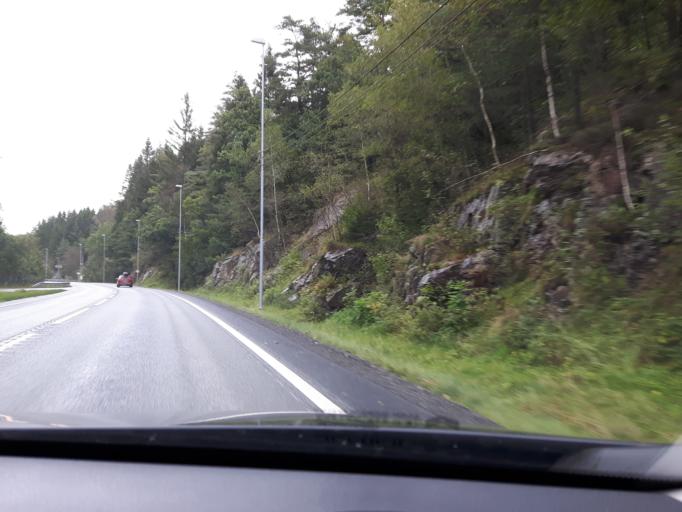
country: NO
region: Vest-Agder
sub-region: Marnardal
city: Helland
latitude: 58.0842
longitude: 7.6182
